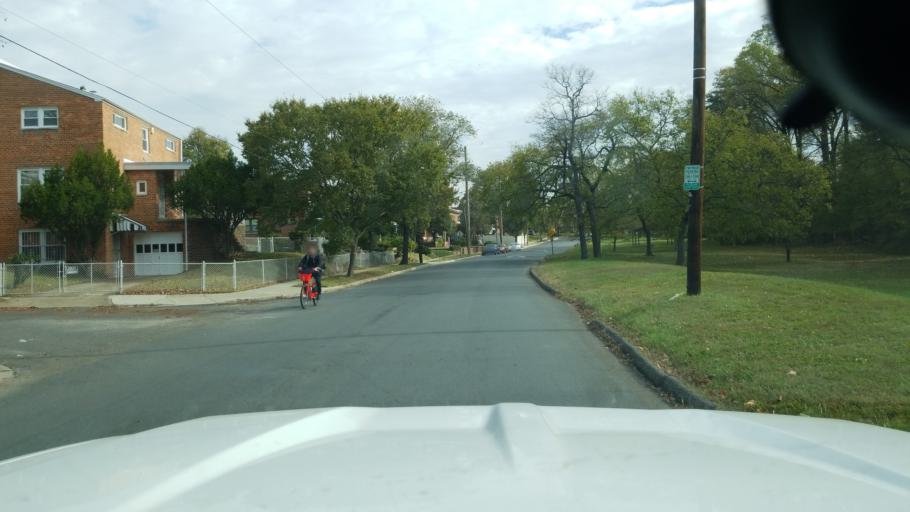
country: US
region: Maryland
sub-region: Prince George's County
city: Chillum
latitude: 38.9533
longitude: -76.9937
